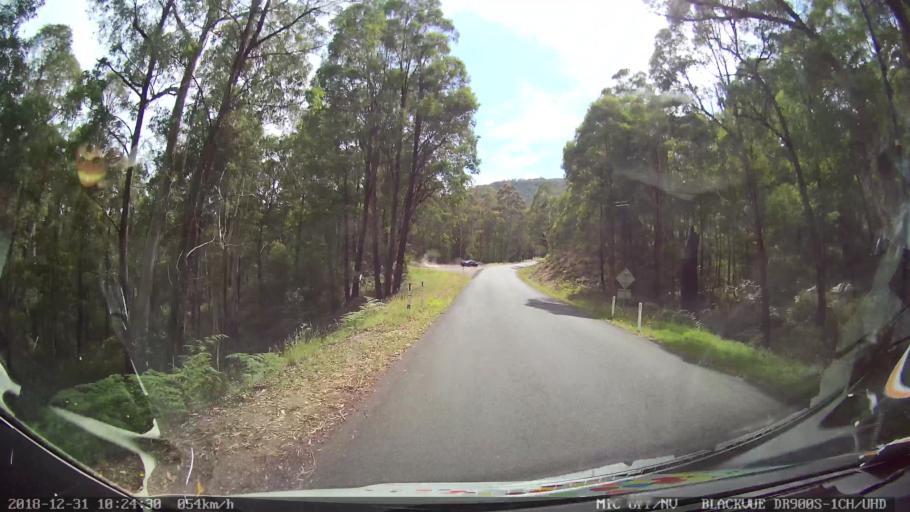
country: AU
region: New South Wales
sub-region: Snowy River
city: Jindabyne
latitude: -36.5120
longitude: 148.1406
